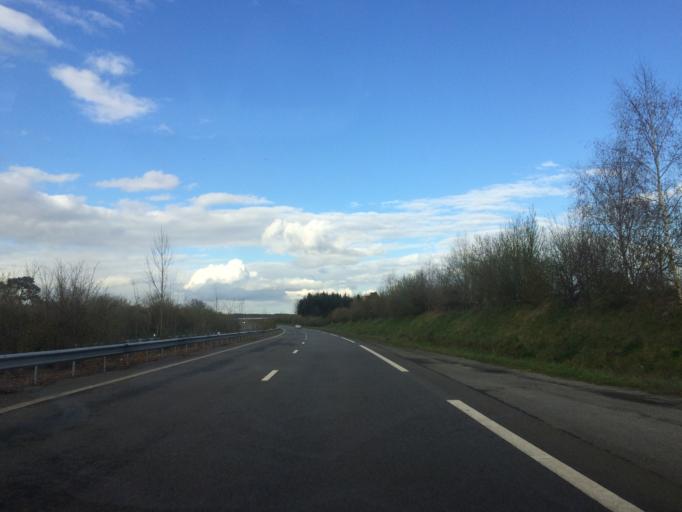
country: FR
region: Brittany
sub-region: Departement d'Ille-et-Vilaine
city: Guipry
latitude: 47.8513
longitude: -1.8982
